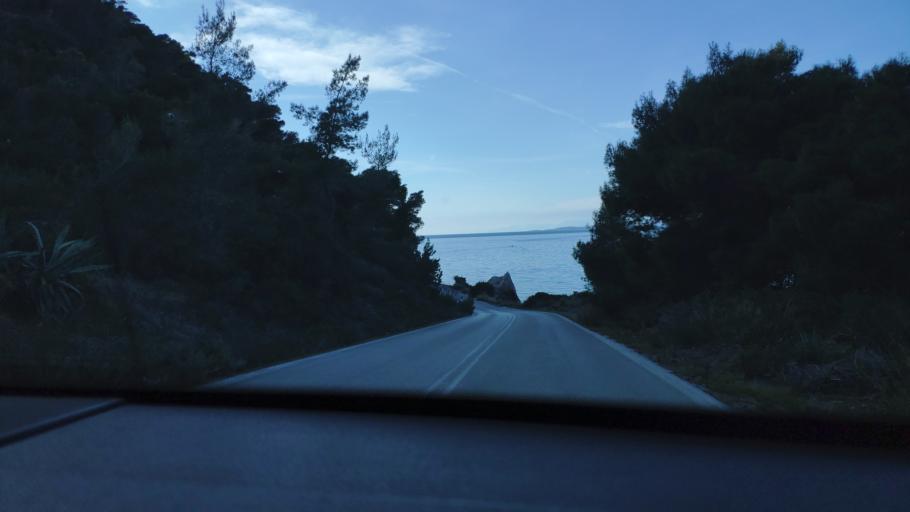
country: GR
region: Peloponnese
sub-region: Nomos Korinthias
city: Agioi Theodoroi
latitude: 38.0590
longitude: 23.1119
